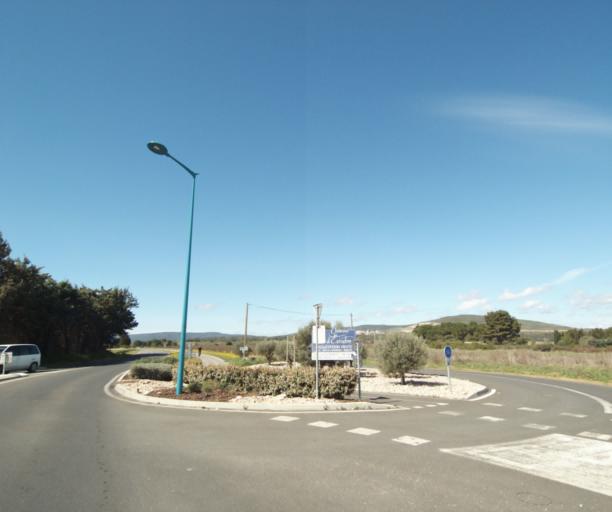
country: FR
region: Languedoc-Roussillon
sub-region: Departement de l'Herault
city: Villeneuve-les-Maguelone
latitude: 43.5292
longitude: 3.8461
